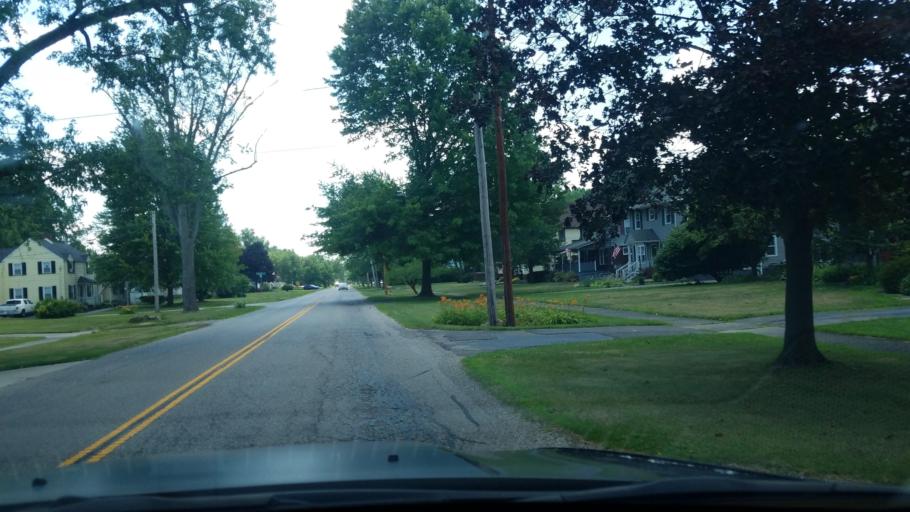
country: US
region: Ohio
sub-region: Trumbull County
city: Bolindale
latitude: 41.2326
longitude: -80.7850
